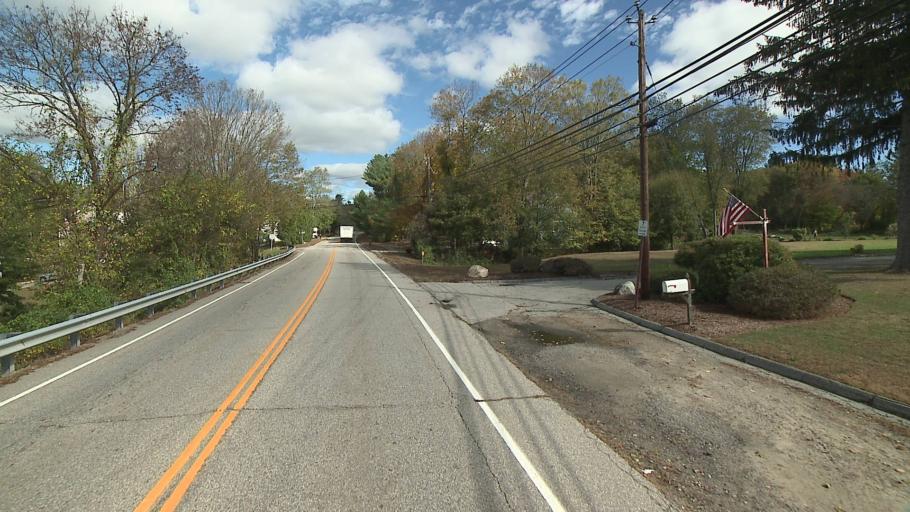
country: US
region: Connecticut
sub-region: Windham County
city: Killingly Center
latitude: 41.8678
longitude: -71.8809
